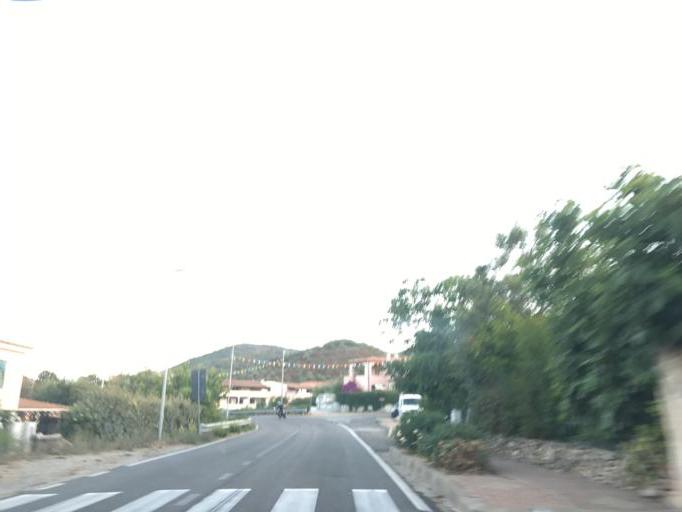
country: IT
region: Sardinia
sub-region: Provincia di Olbia-Tempio
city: San Teodoro
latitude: 40.7515
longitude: 9.6472
